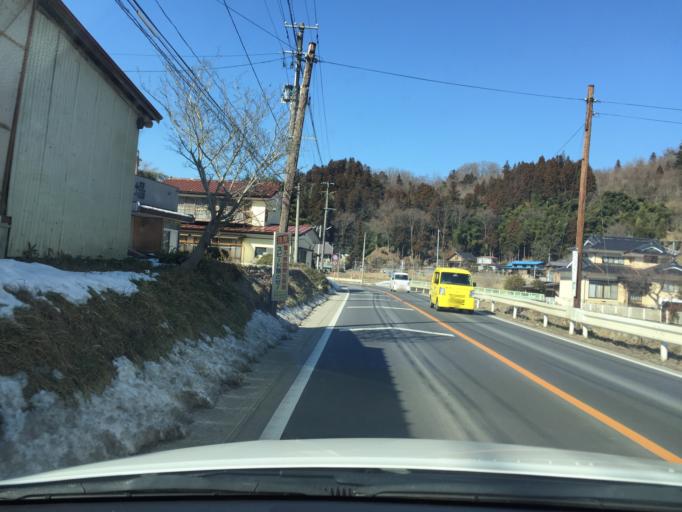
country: JP
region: Fukushima
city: Yanagawamachi-saiwaicho
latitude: 37.7613
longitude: 140.6286
